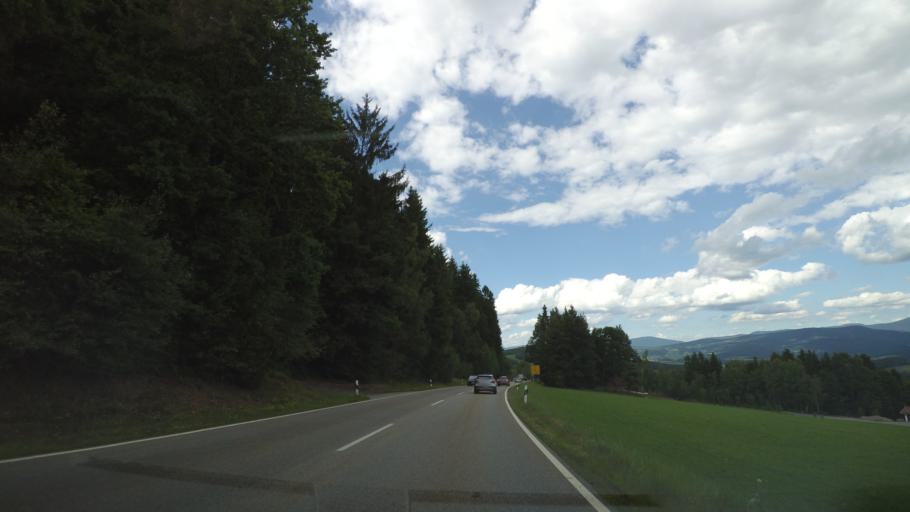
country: DE
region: Bavaria
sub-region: Lower Bavaria
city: Kollnburg
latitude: 49.0385
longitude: 12.8637
